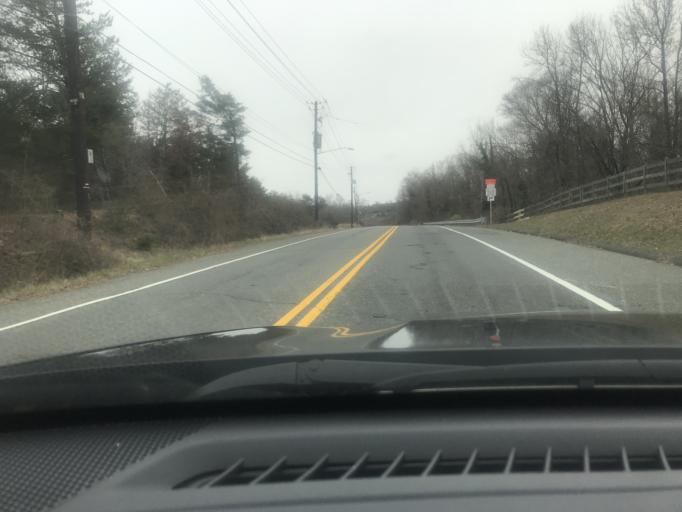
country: US
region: Maryland
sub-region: Prince George's County
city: Friendly
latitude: 38.7781
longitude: -76.9759
